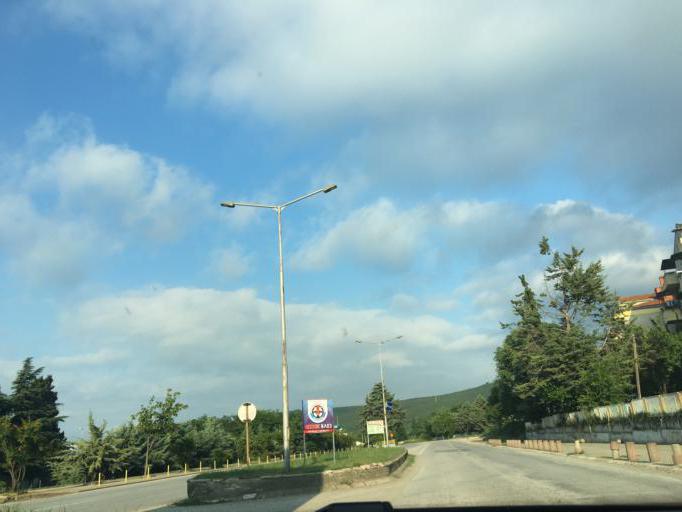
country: MK
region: Valandovo
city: Valandovo
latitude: 41.3155
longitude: 22.5592
